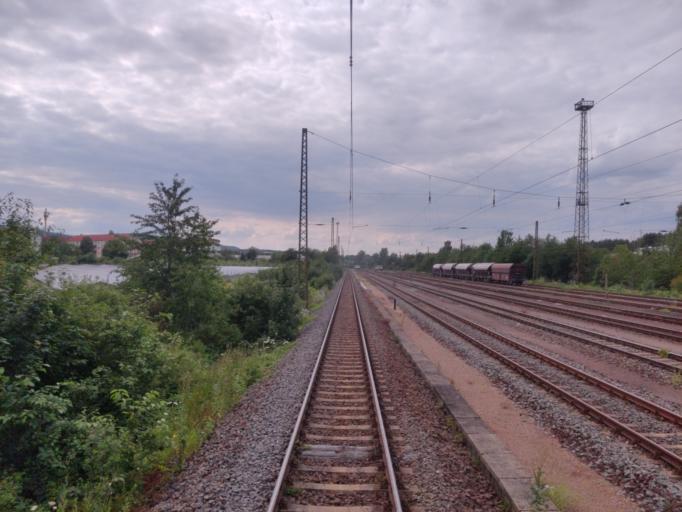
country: DE
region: Saxony-Anhalt
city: Blankenburg
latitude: 51.8058
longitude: 10.9508
